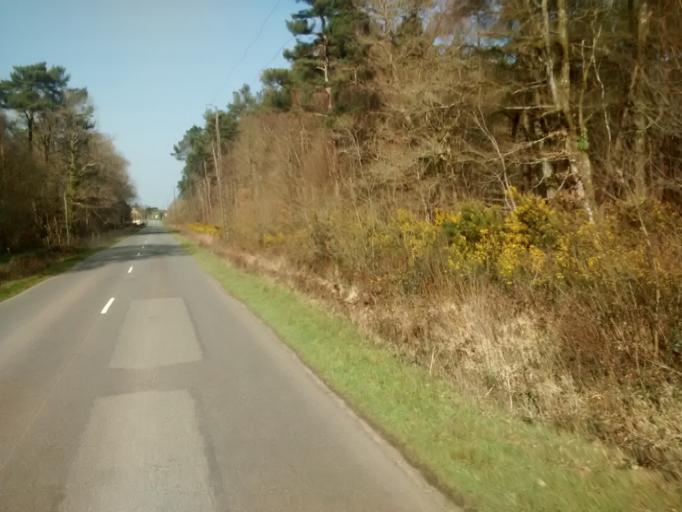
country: FR
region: Brittany
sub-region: Departement d'Ille-et-Vilaine
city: Paimpont
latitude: 48.0339
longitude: -2.1784
